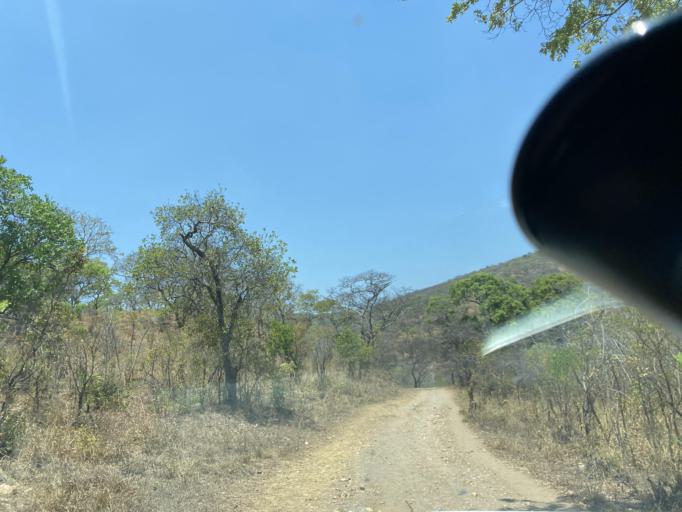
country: ZM
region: Lusaka
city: Kafue
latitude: -15.8067
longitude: 28.4306
